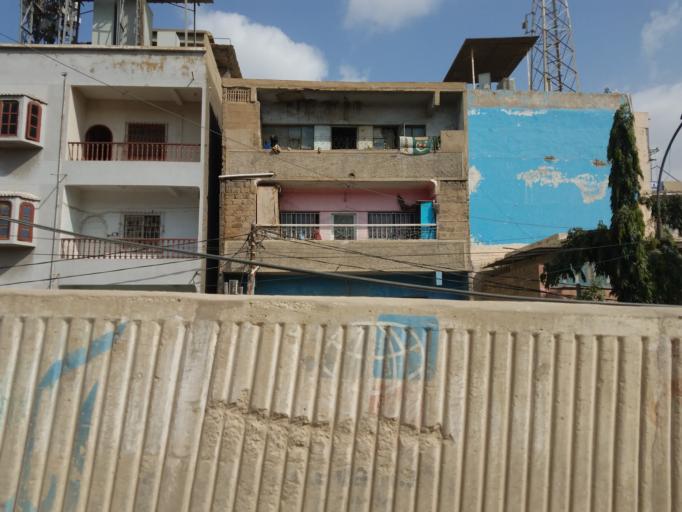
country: PK
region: Sindh
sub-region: Karachi District
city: Karachi
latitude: 24.9137
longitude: 67.0511
